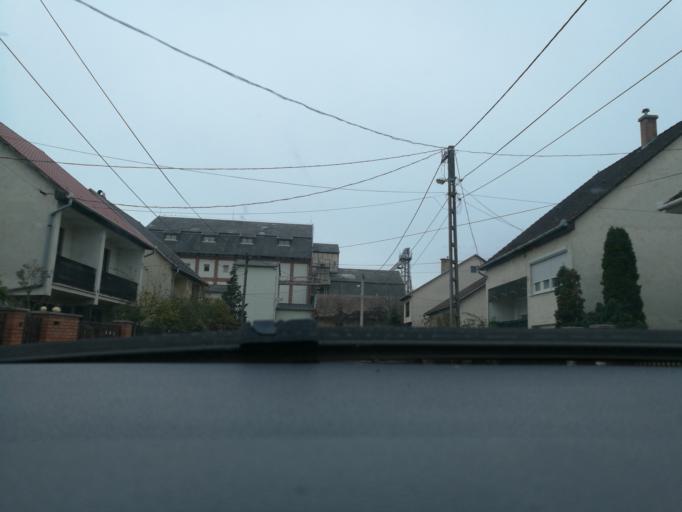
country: HU
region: Nograd
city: Szecseny
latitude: 48.0835
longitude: 19.5256
